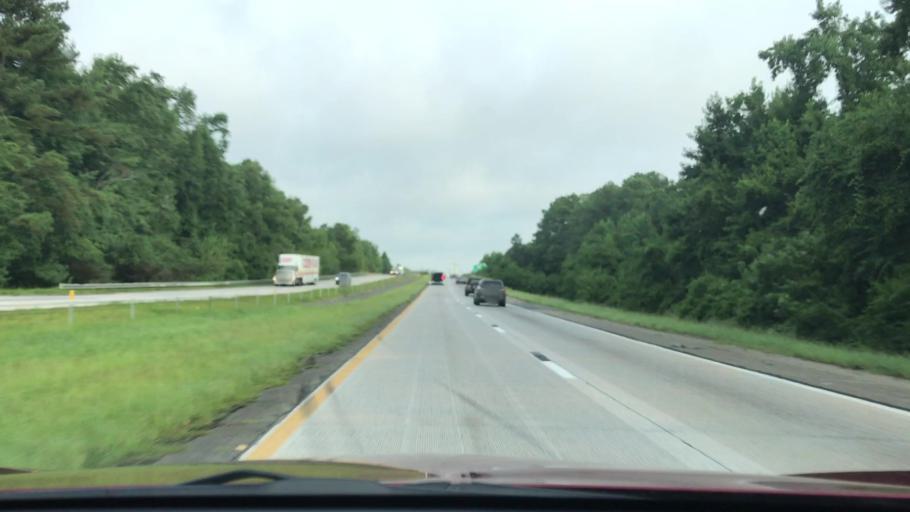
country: US
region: South Carolina
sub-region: Orangeburg County
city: Holly Hill
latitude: 33.2297
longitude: -80.4391
